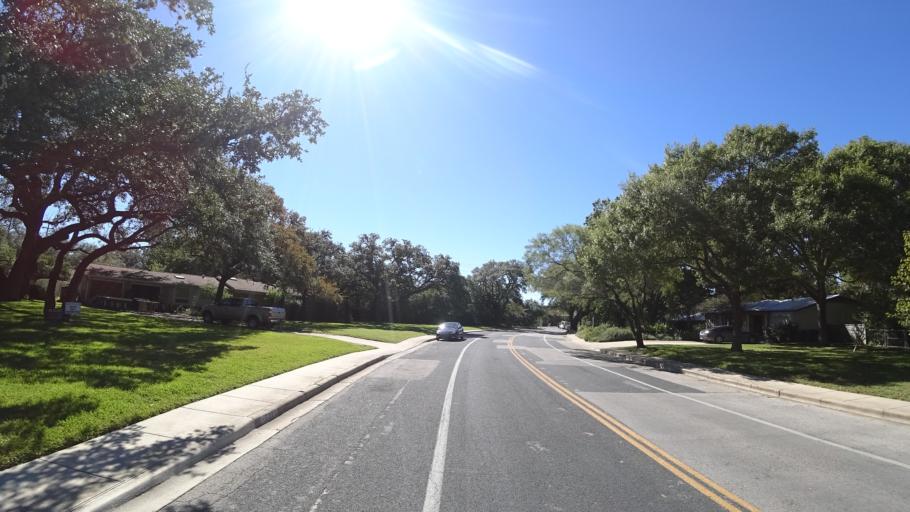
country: US
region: Texas
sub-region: Travis County
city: West Lake Hills
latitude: 30.3359
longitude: -97.7483
